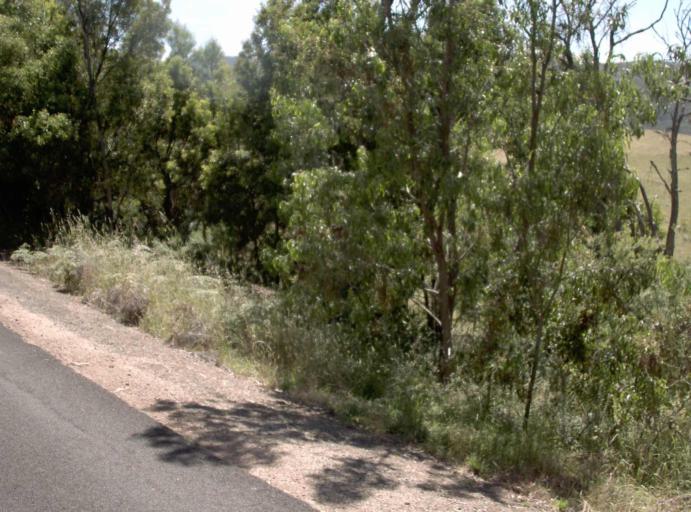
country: AU
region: Victoria
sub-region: East Gippsland
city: Lakes Entrance
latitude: -37.4228
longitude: 148.2025
